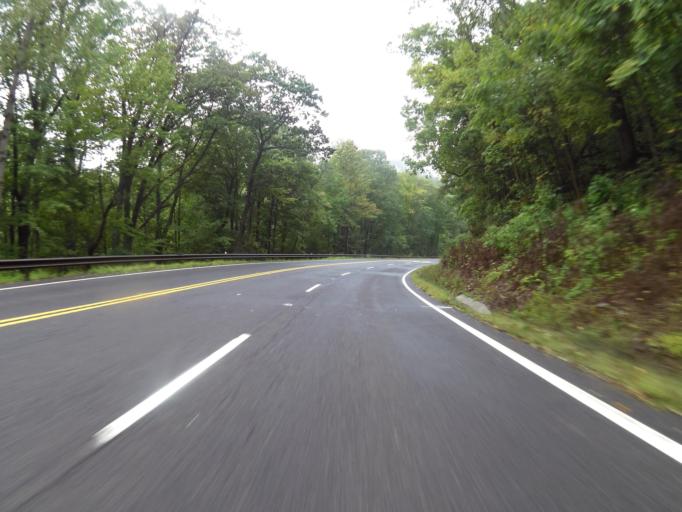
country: US
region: Virginia
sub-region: Page County
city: Luray
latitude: 38.6620
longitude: -78.3059
